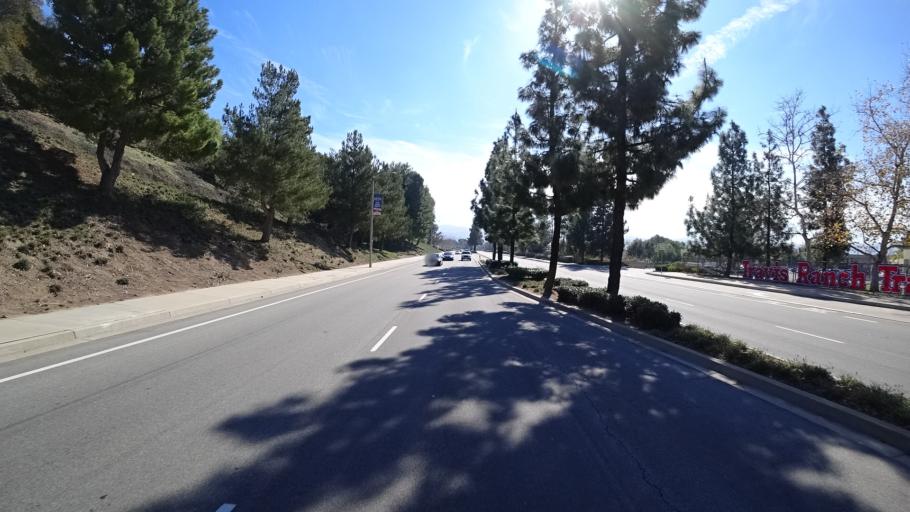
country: US
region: California
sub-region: Orange County
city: Yorba Linda
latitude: 33.8868
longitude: -117.7586
